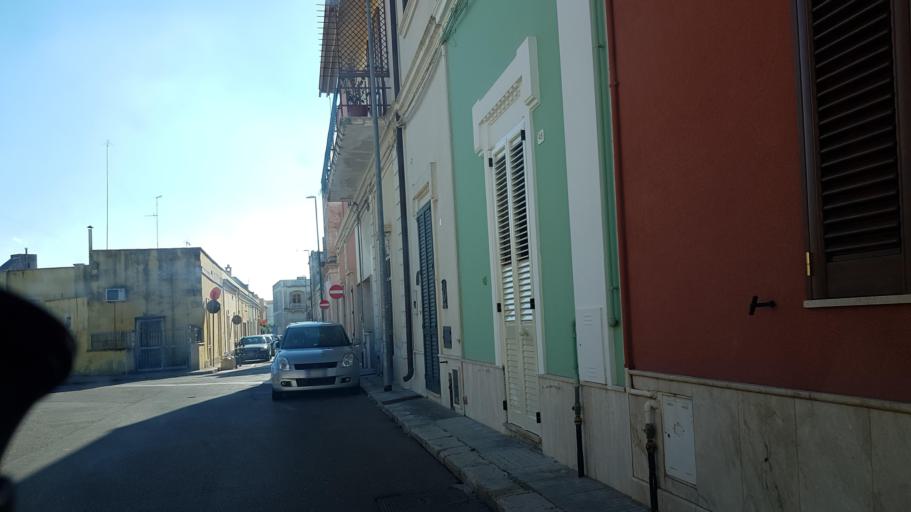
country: IT
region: Apulia
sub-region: Provincia di Lecce
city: Arnesano
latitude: 40.3355
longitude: 18.0908
